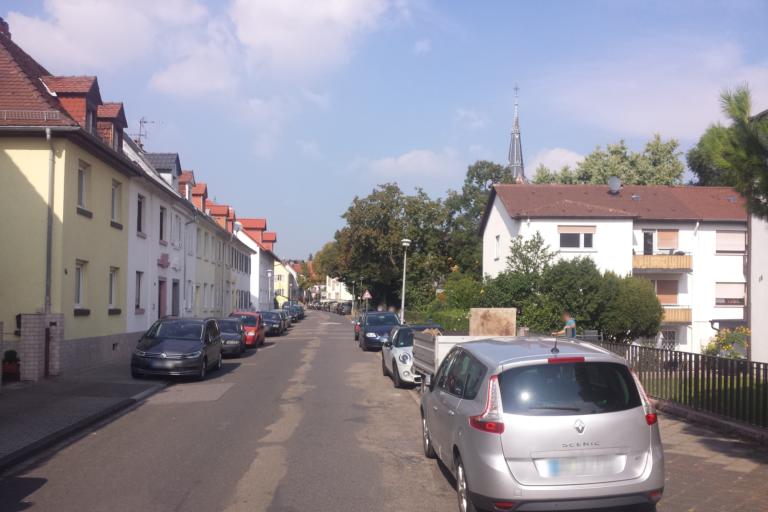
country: DE
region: Baden-Wuerttemberg
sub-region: Karlsruhe Region
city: Ilvesheim
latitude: 49.4850
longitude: 8.5335
